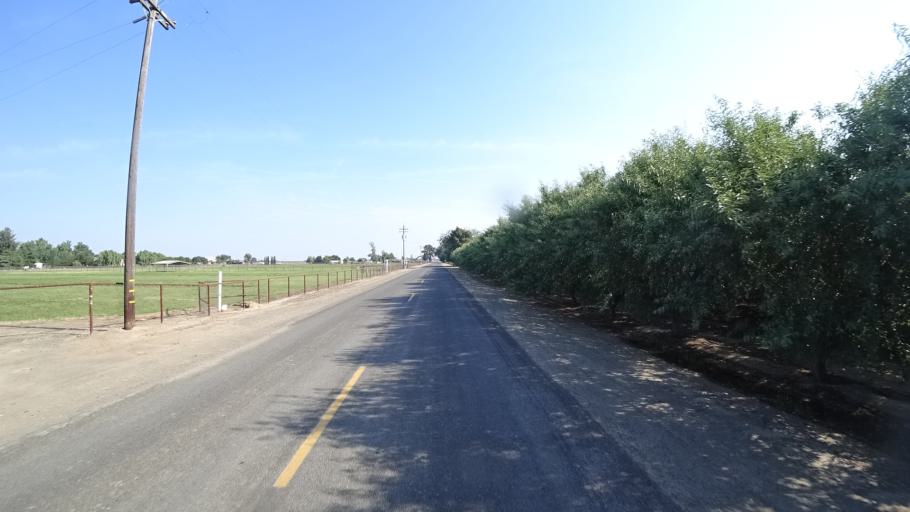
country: US
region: California
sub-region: Fresno County
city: Riverdale
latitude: 36.3695
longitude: -119.8161
